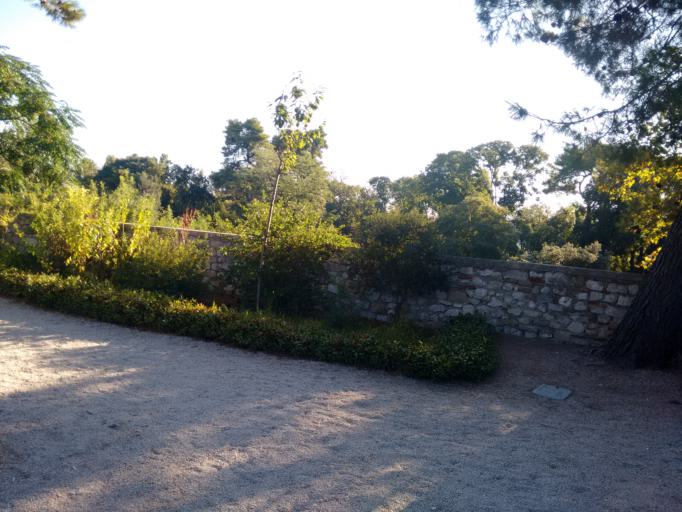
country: HR
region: Zadarska
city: Zadar
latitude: 44.1120
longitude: 15.2300
